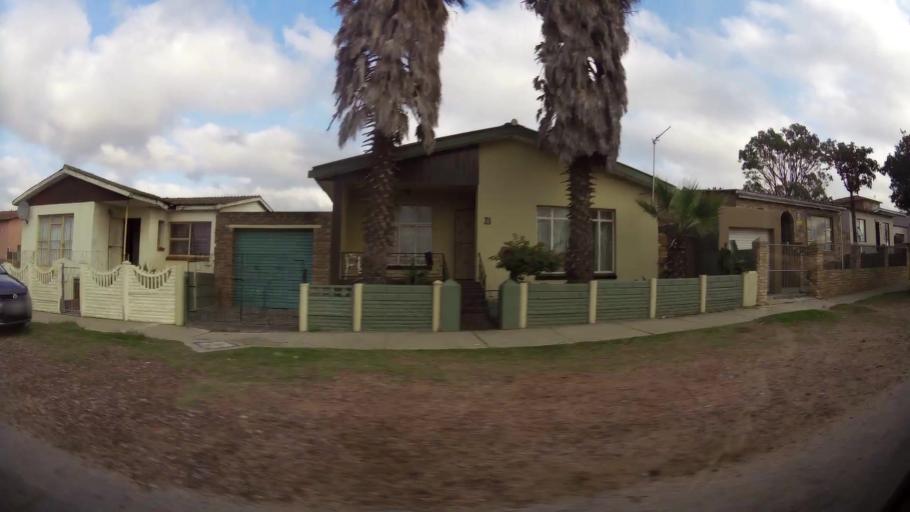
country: ZA
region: Eastern Cape
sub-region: Nelson Mandela Bay Metropolitan Municipality
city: Port Elizabeth
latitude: -33.9134
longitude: 25.5500
